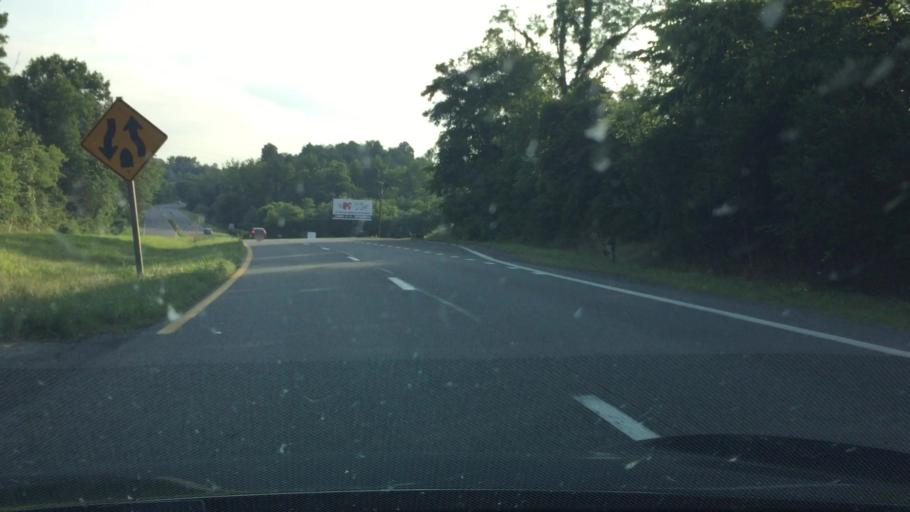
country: US
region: Virginia
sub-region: Pulaski County
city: Fairlawn
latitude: 37.1377
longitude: -80.6124
